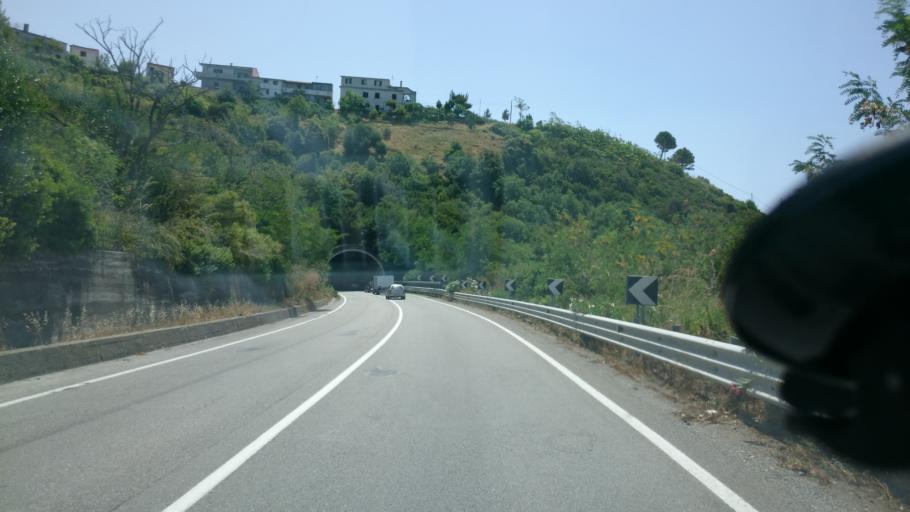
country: IT
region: Calabria
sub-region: Provincia di Cosenza
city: Cittadella del Capo
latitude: 39.5474
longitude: 15.8830
